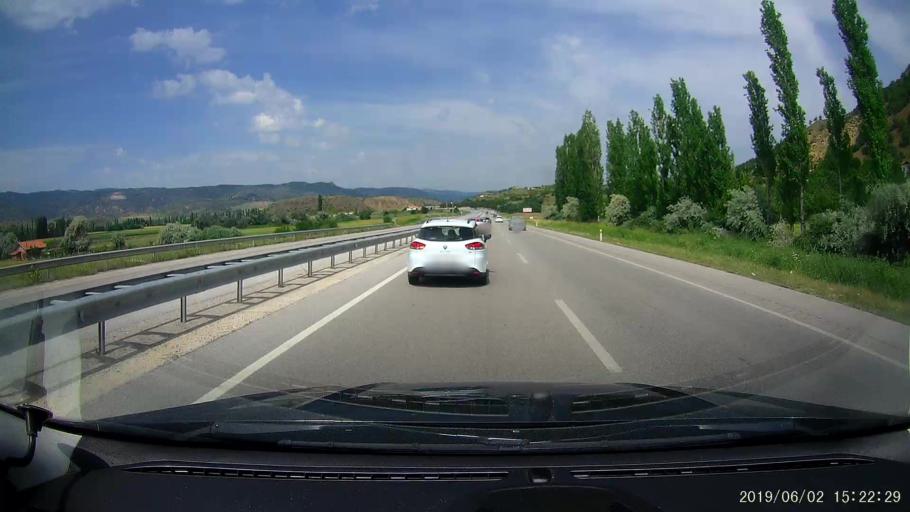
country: TR
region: Corum
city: Osmancik
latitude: 40.9830
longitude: 34.9588
